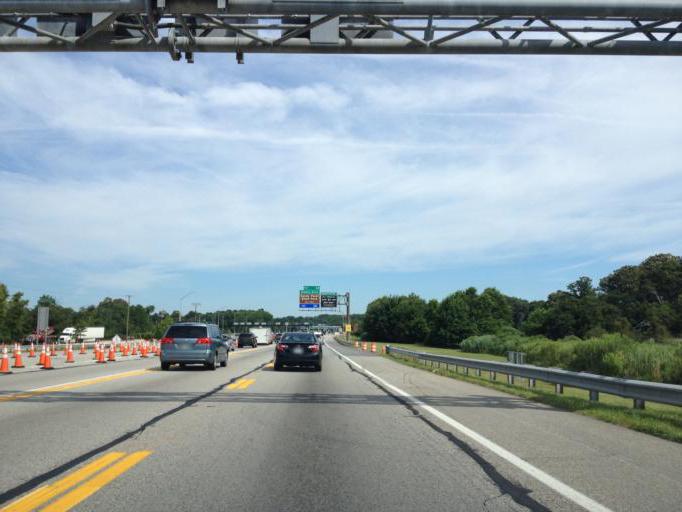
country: US
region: Maryland
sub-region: Anne Arundel County
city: Cape Saint Claire
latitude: 39.0095
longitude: -76.4044
